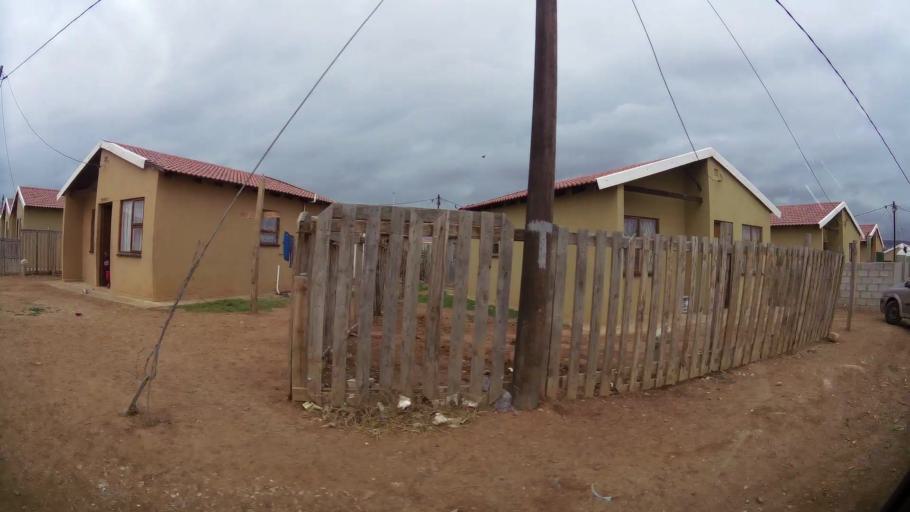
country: ZA
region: Eastern Cape
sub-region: Nelson Mandela Bay Metropolitan Municipality
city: Port Elizabeth
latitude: -33.8838
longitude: 25.5542
